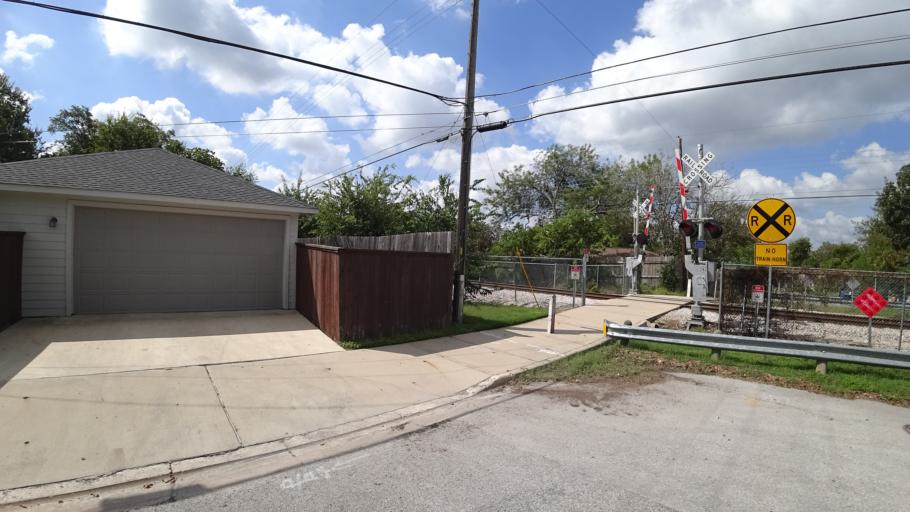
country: US
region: Texas
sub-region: Travis County
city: Austin
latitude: 30.3555
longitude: -97.7219
